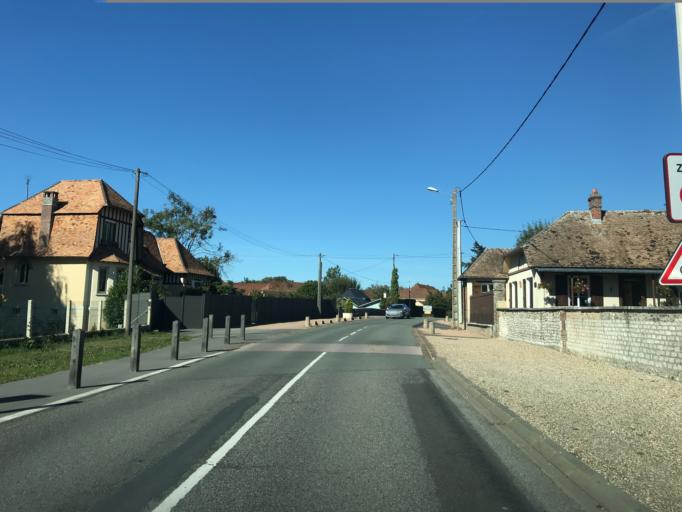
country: FR
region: Haute-Normandie
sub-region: Departement de l'Eure
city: Le Vaudreuil
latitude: 49.2518
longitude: 1.2085
